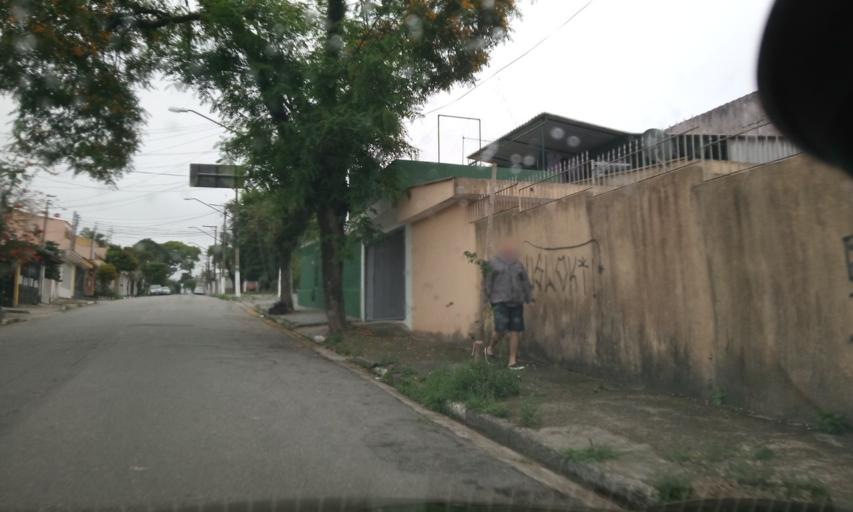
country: BR
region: Sao Paulo
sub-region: Sao Bernardo Do Campo
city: Sao Bernardo do Campo
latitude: -23.6763
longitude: -46.5627
